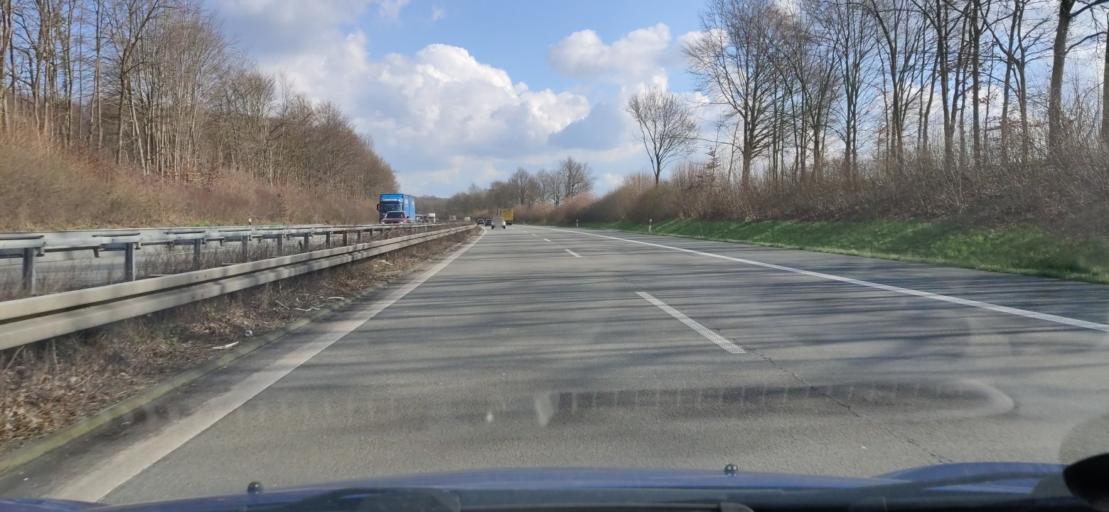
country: DE
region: North Rhine-Westphalia
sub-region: Regierungsbezirk Munster
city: Tecklenburg
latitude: 52.2531
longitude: 7.7874
